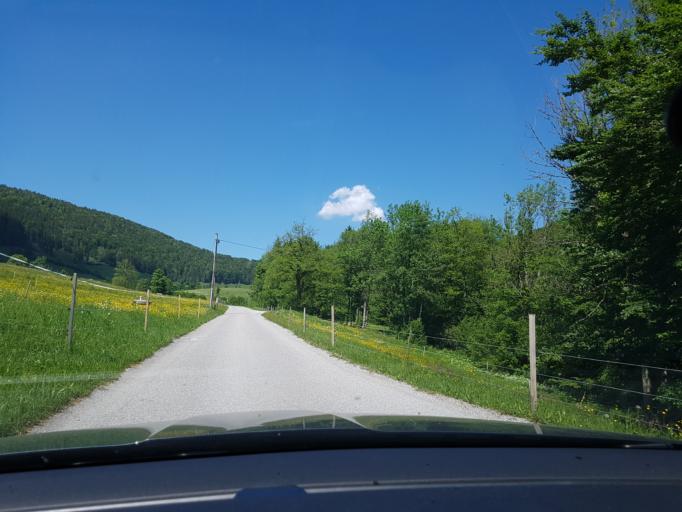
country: AT
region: Salzburg
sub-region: Politischer Bezirk Salzburg-Umgebung
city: Koppl
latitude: 47.7875
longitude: 13.1249
